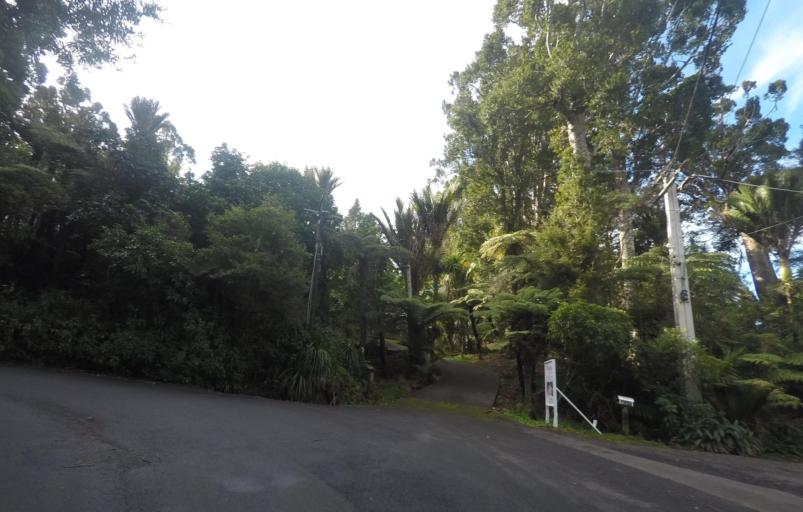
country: NZ
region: Auckland
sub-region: Auckland
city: Titirangi
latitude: -36.9396
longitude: 174.6432
